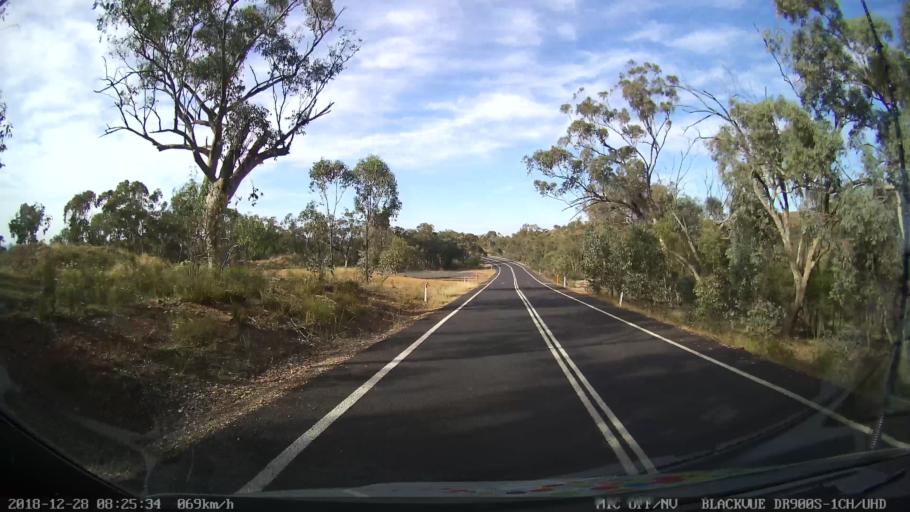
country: AU
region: New South Wales
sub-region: Blayney
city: Blayney
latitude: -33.9274
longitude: 149.3519
